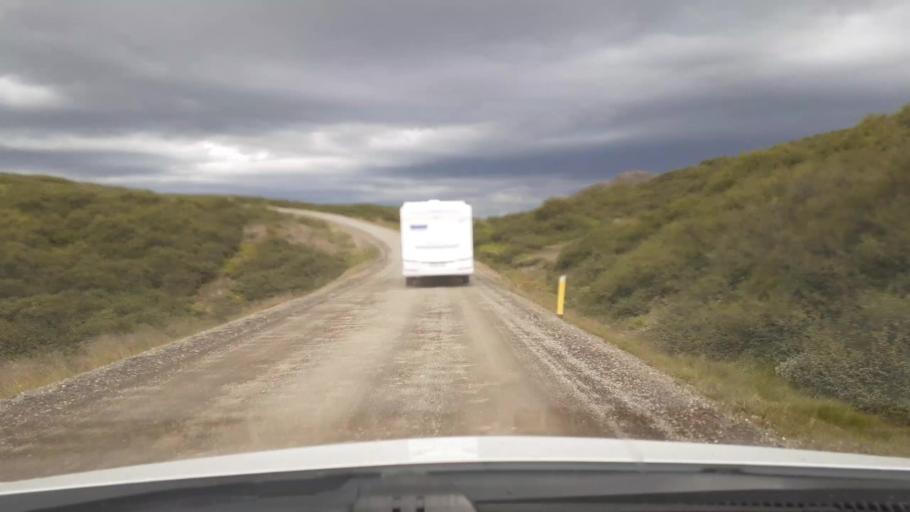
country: IS
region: West
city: Borgarnes
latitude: 64.5552
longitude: -21.6236
